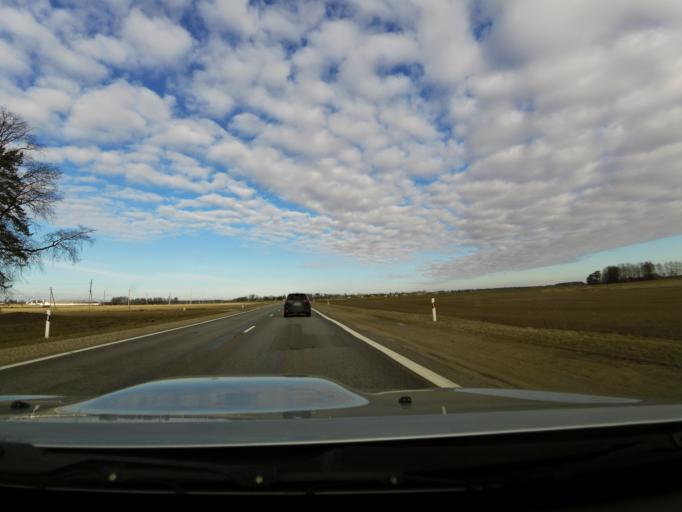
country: LT
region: Siauliu apskritis
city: Pakruojis
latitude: 55.7909
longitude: 24.0307
